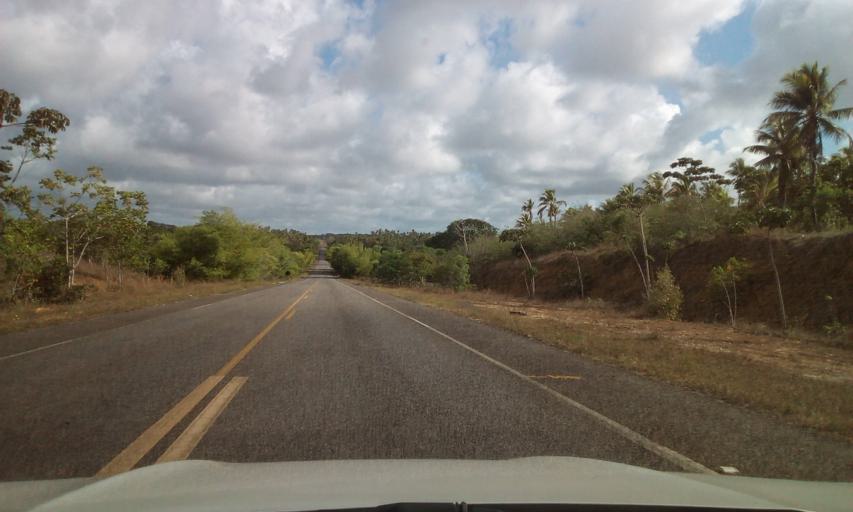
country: BR
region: Sergipe
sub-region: Indiaroba
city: Indiaroba
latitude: -11.6343
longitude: -37.5391
